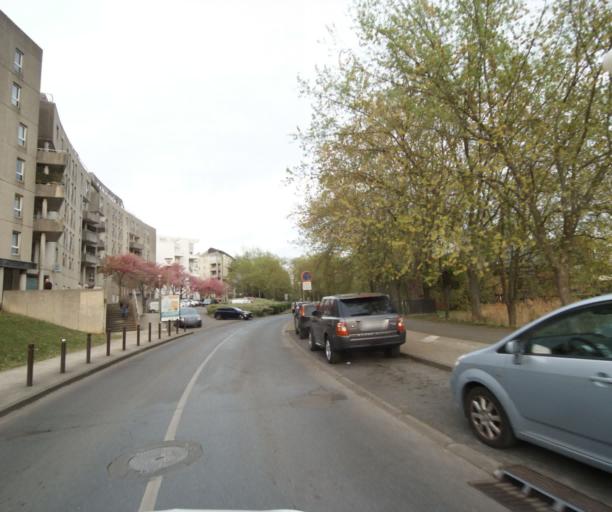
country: FR
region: Ile-de-France
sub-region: Departement de Seine-et-Marne
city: Torcy
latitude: 48.8436
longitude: 2.6448
